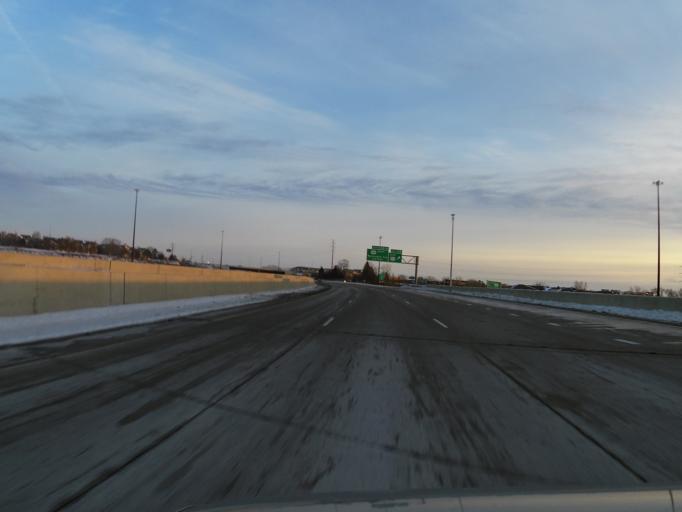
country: US
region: Minnesota
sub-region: Hennepin County
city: Eden Prairie
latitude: 44.8651
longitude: -93.4303
